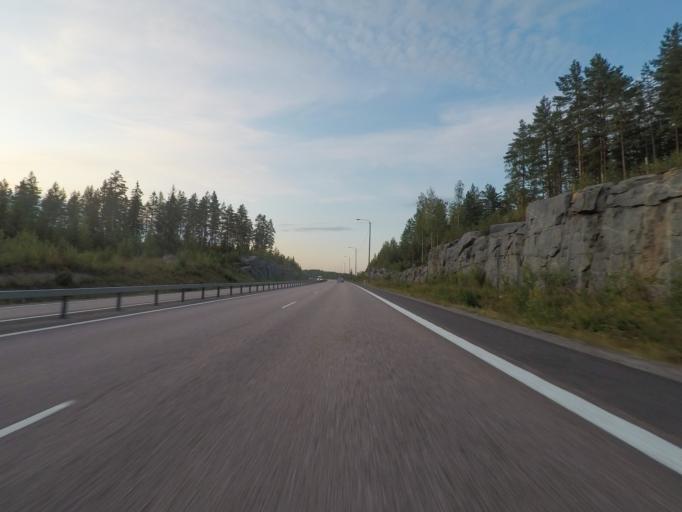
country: FI
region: Central Finland
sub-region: Jyvaeskylae
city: Saeynaetsalo
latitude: 62.1684
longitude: 25.9042
